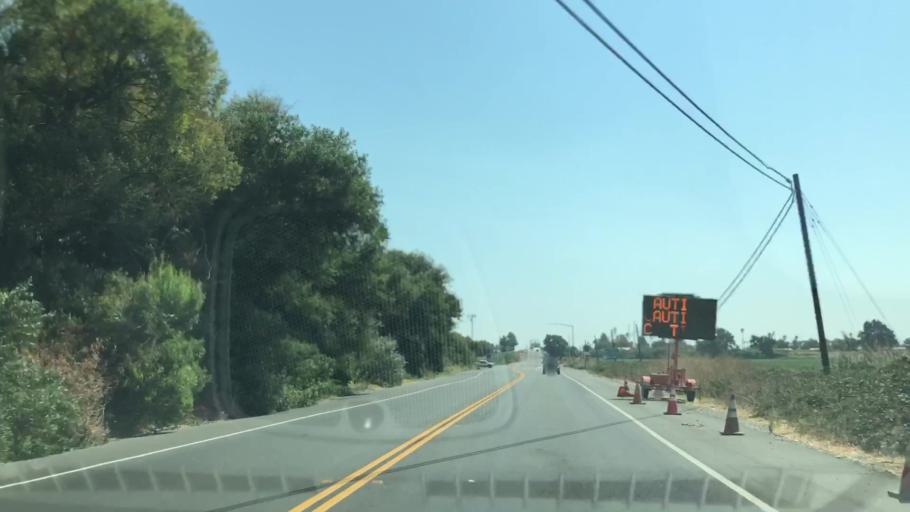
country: US
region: California
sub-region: Solano County
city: Rio Vista
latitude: 38.1294
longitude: -121.5882
